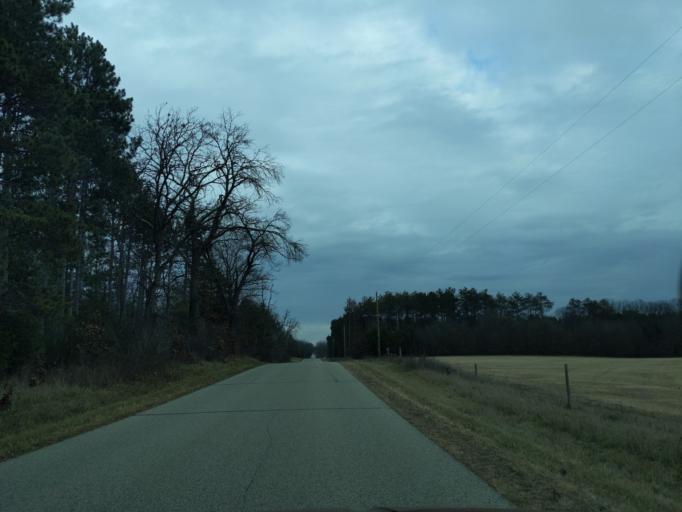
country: US
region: Wisconsin
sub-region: Waushara County
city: Wautoma
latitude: 44.0439
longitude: -89.2844
